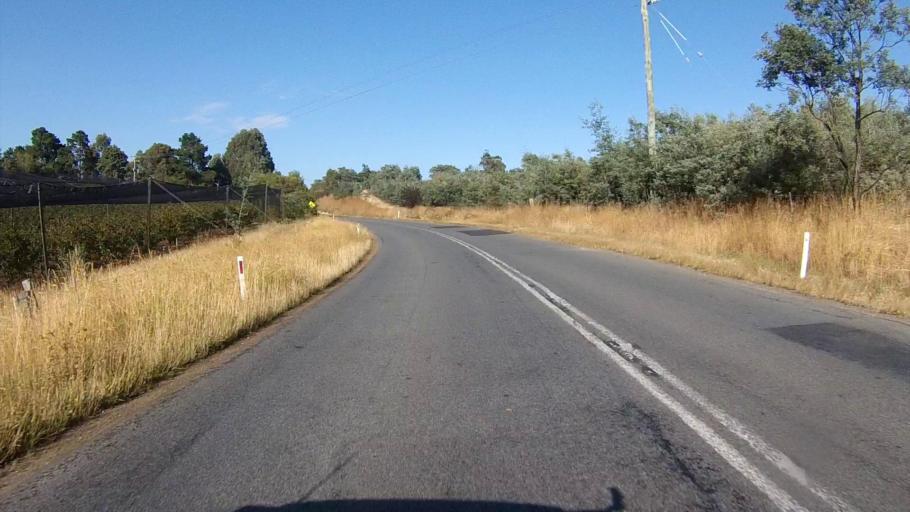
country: AU
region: Tasmania
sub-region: Derwent Valley
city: New Norfolk
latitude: -42.7619
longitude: 147.1344
